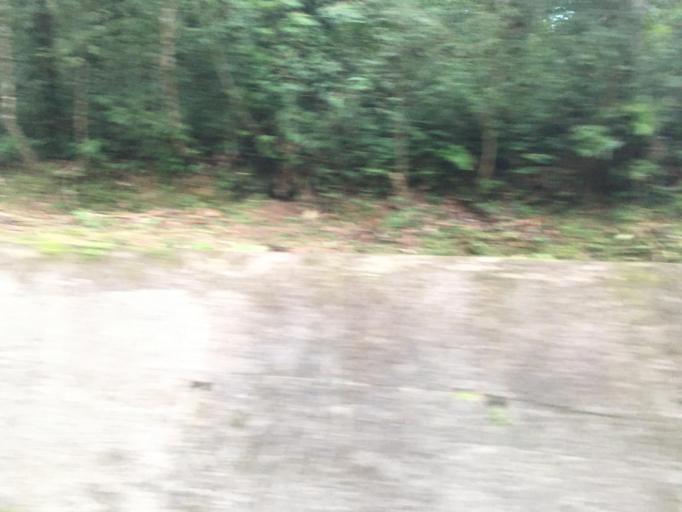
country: TW
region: Taiwan
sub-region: Yilan
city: Yilan
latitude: 24.7578
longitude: 121.5927
